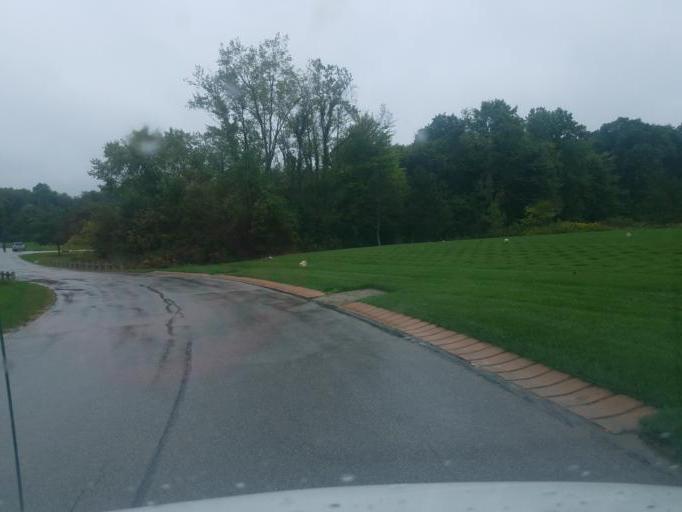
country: US
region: Ohio
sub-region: Wayne County
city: Rittman
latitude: 40.9978
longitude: -81.8109
